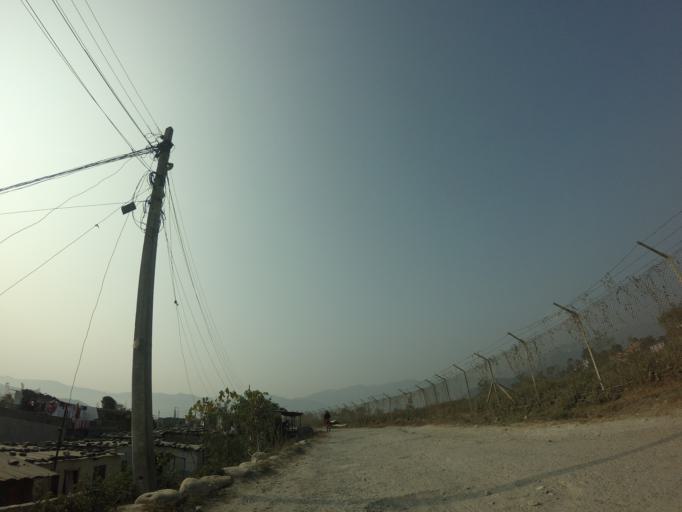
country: NP
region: Western Region
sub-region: Gandaki Zone
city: Pokhara
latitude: 28.2031
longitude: 83.9858
